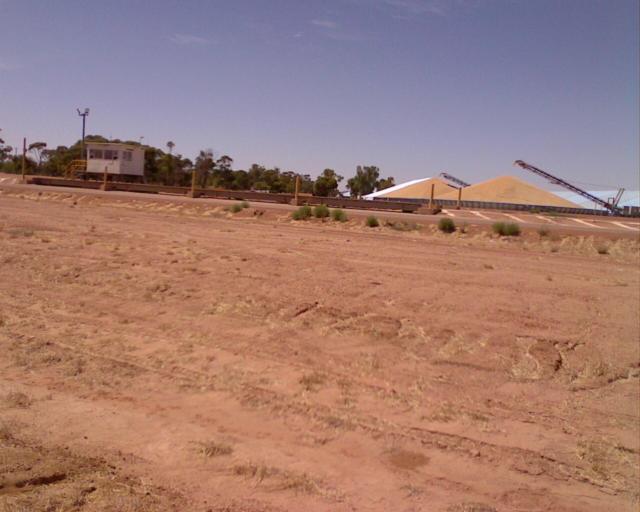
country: AU
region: Western Australia
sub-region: Moora
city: Moora
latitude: -30.3002
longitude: 116.0558
